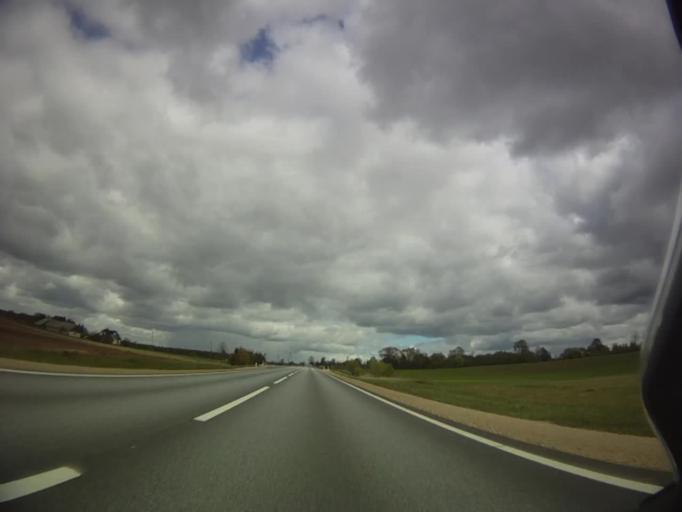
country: LV
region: Sigulda
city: Sigulda
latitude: 57.2512
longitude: 24.8535
